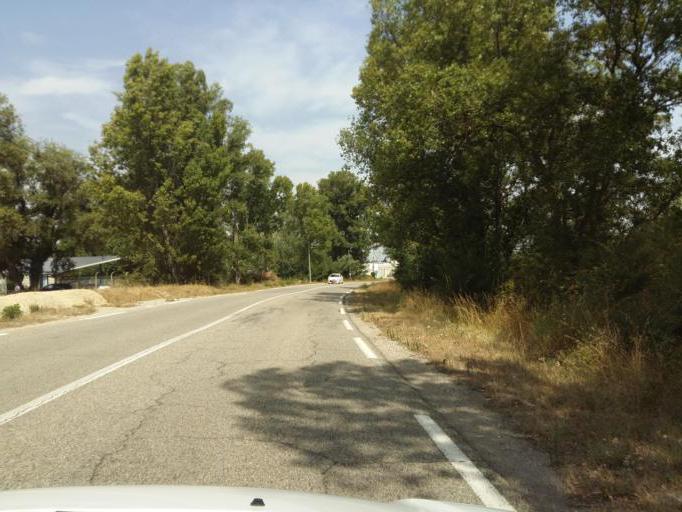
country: FR
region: Provence-Alpes-Cote d'Azur
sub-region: Departement du Vaucluse
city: Bollene
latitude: 44.3081
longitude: 4.7358
